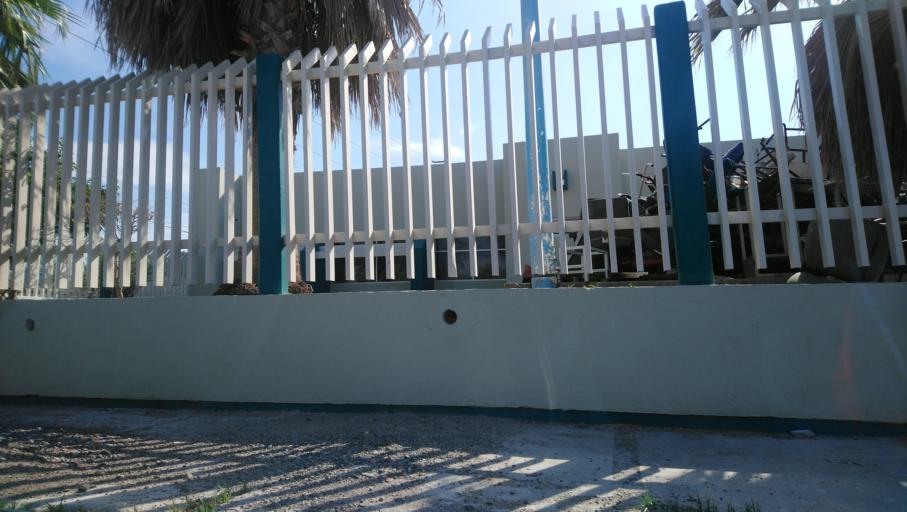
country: MX
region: Oaxaca
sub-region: Salina Cruz
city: Salina Cruz
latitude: 16.2022
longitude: -95.2010
